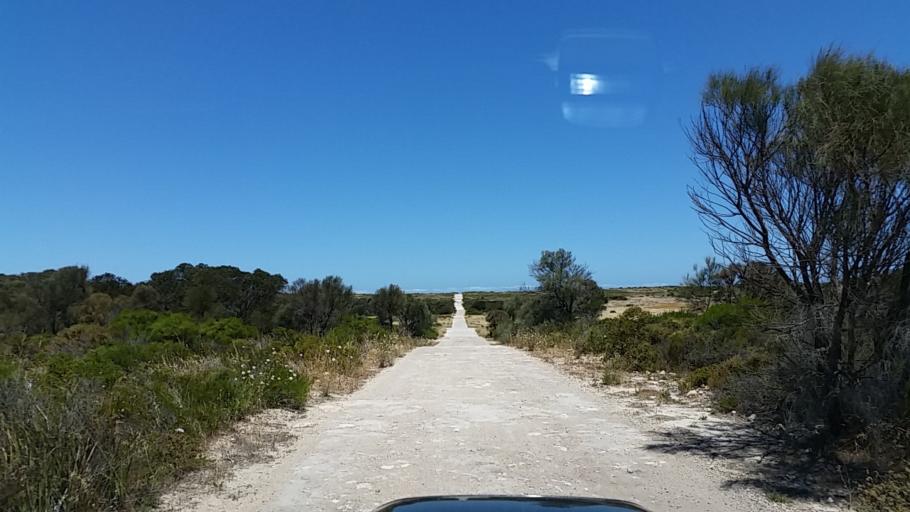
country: AU
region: South Australia
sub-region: Yorke Peninsula
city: Honiton
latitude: -35.2225
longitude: 137.0695
